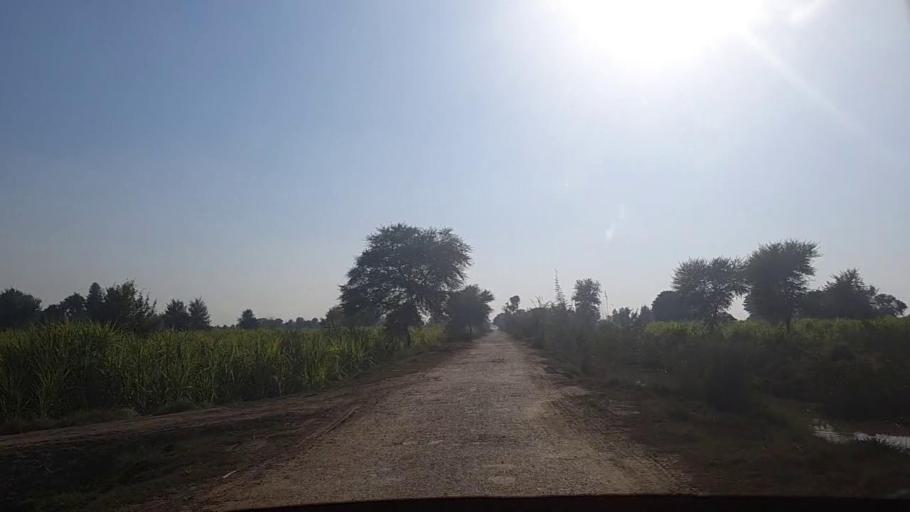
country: PK
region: Sindh
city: Gambat
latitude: 27.3692
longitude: 68.4626
